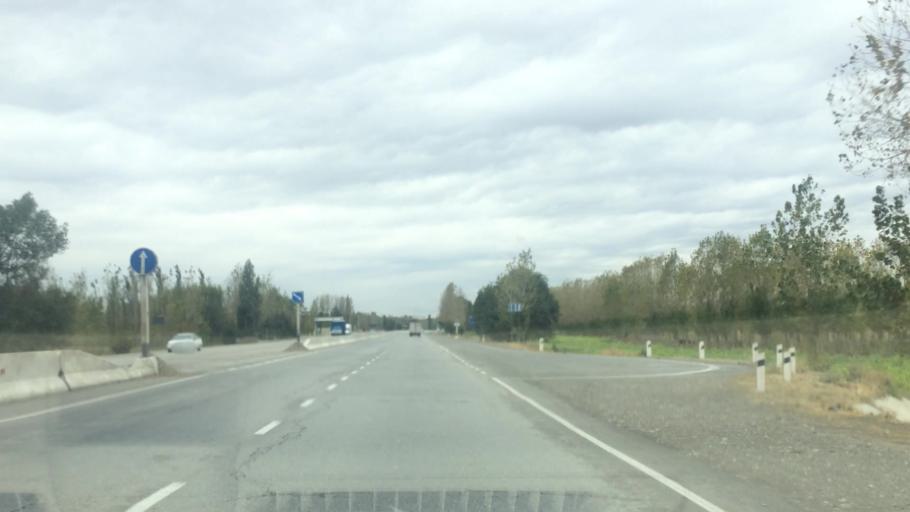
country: UZ
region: Jizzax
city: Jizzax
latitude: 39.9640
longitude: 67.5500
